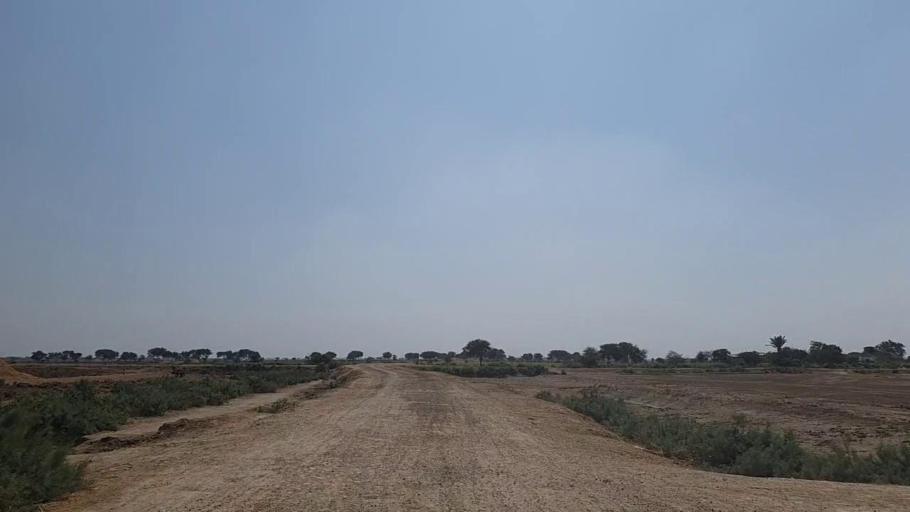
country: PK
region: Sindh
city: Jati
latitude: 24.5376
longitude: 68.3152
